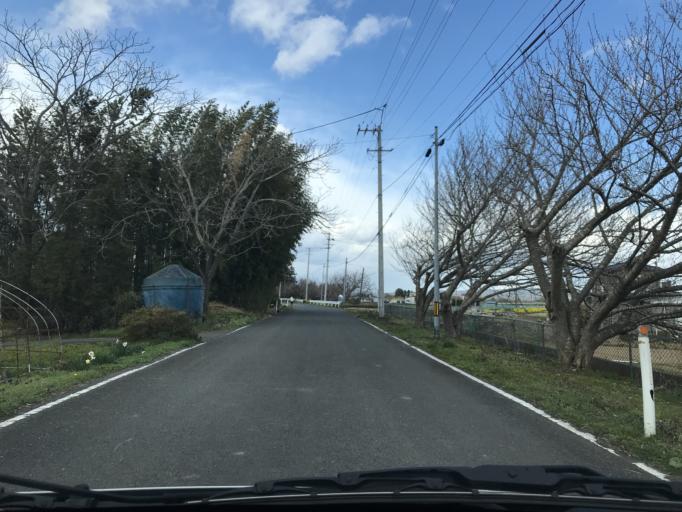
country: JP
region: Miyagi
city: Wakuya
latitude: 38.6478
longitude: 141.2055
